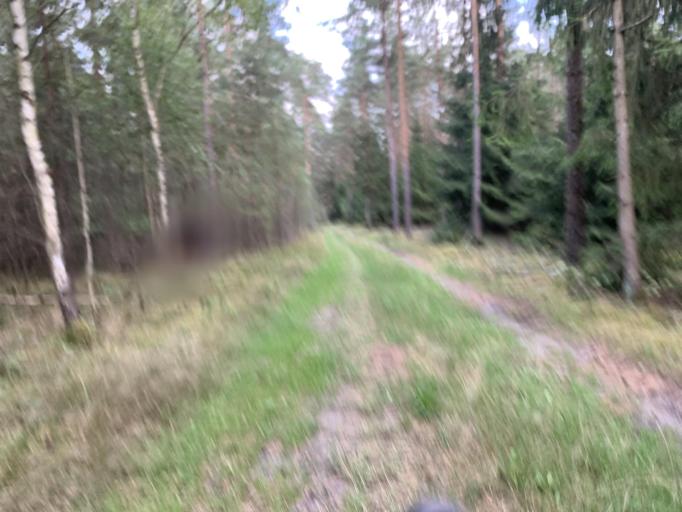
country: DE
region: Lower Saxony
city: Reinstorf
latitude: 53.2155
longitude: 10.6057
